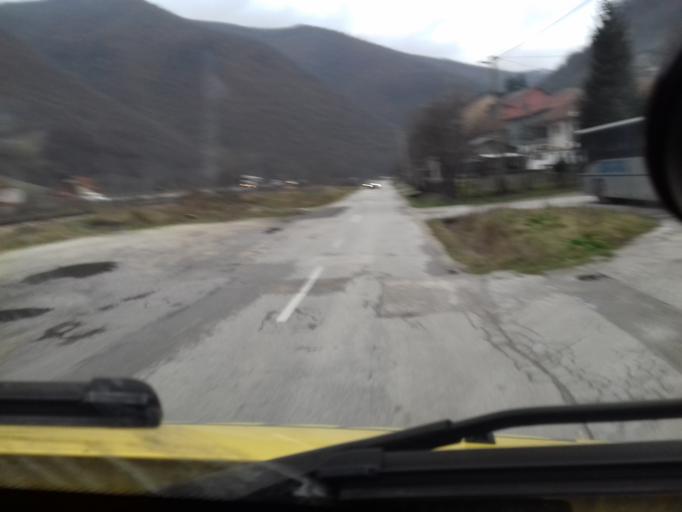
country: BA
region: Federation of Bosnia and Herzegovina
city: Zenica
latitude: 44.1520
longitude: 17.9615
